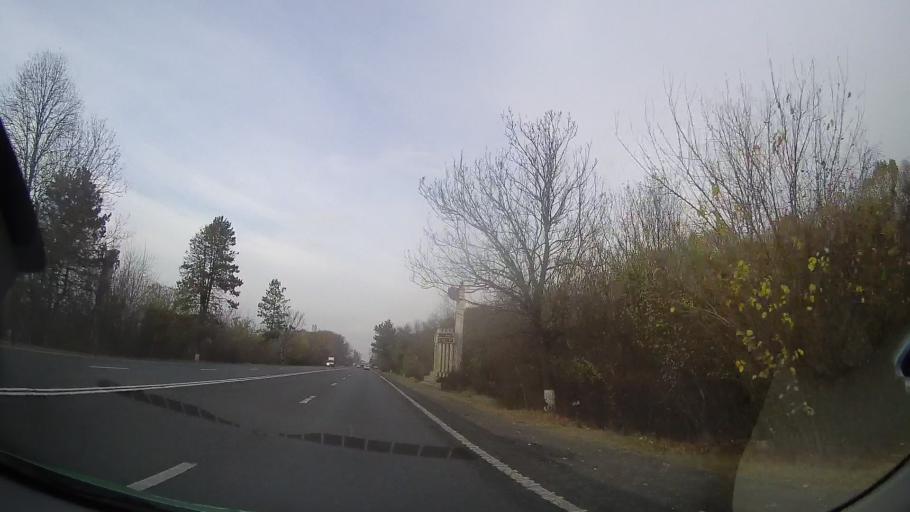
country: RO
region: Prahova
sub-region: Comuna Gorgota
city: Potigrafu
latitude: 44.7633
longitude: 26.1041
